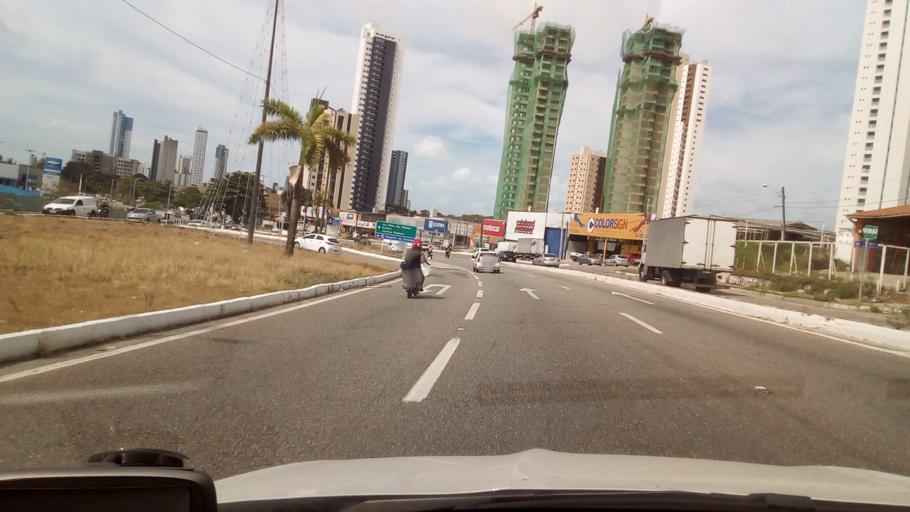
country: BR
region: Paraiba
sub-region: Joao Pessoa
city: Joao Pessoa
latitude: -7.1167
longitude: -34.8421
